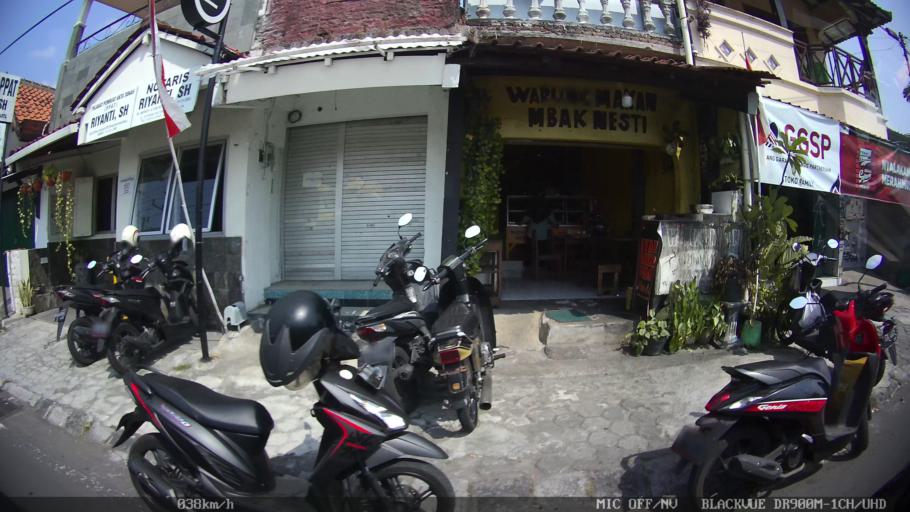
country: ID
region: Daerah Istimewa Yogyakarta
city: Yogyakarta
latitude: -7.8104
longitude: 110.3930
